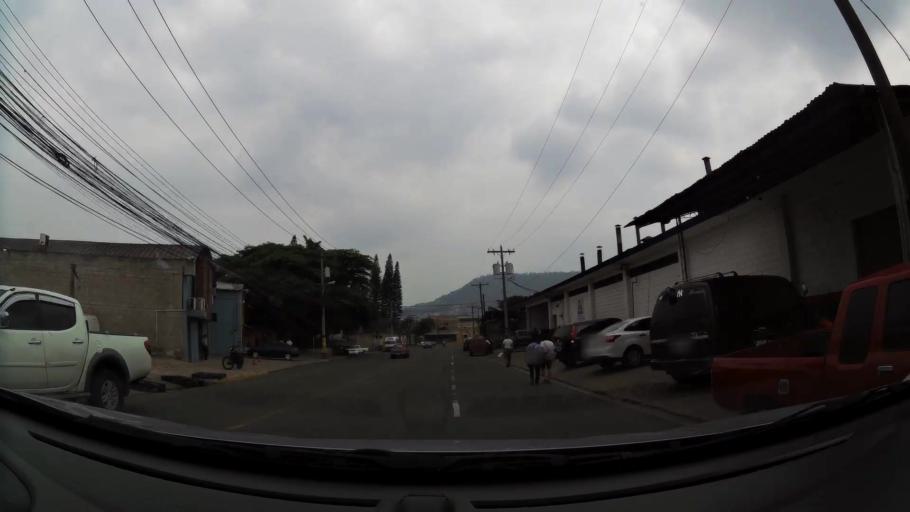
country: HN
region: Francisco Morazan
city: Tegucigalpa
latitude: 14.1024
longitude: -87.1763
